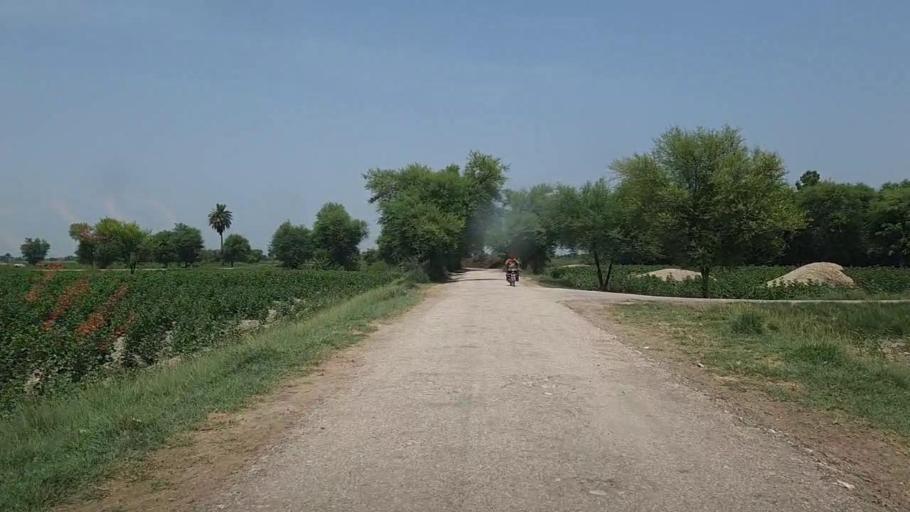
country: PK
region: Sindh
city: Pano Aqil
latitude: 27.8303
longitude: 69.2084
